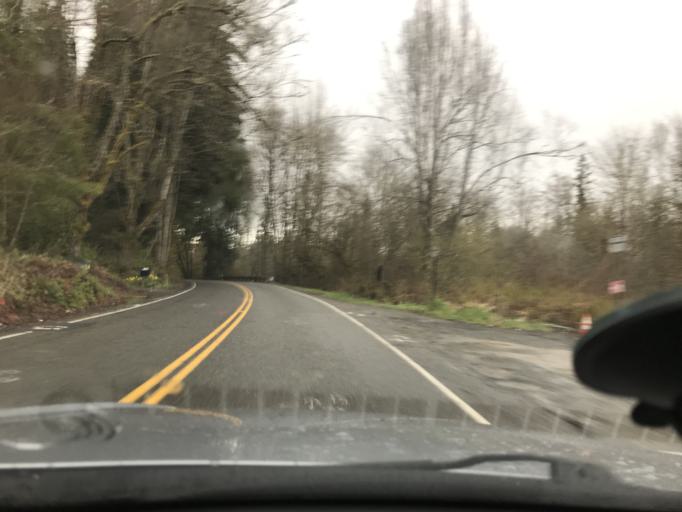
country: US
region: Washington
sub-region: King County
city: Ames Lake
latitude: 47.6559
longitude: -121.9639
